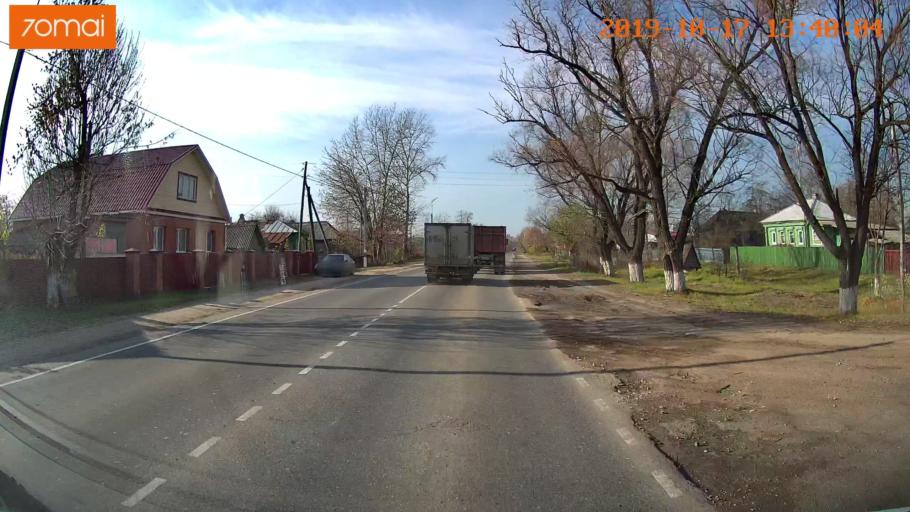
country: RU
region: Rjazan
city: Tuma
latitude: 55.1470
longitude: 40.5776
